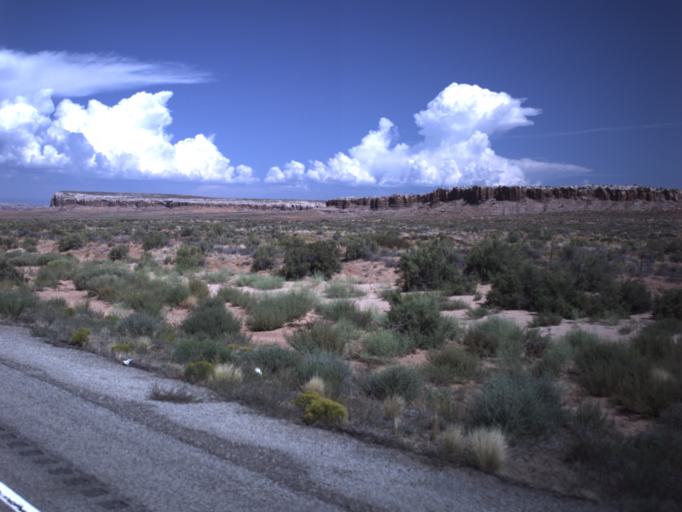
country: US
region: Utah
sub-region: San Juan County
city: Blanding
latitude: 37.1966
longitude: -109.6006
